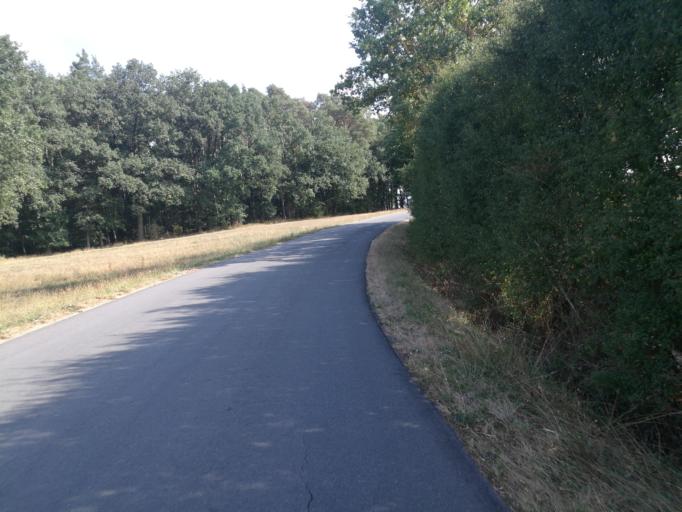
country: DE
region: Bavaria
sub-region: Regierungsbezirk Mittelfranken
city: Veitsbronn
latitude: 49.5059
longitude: 10.9013
